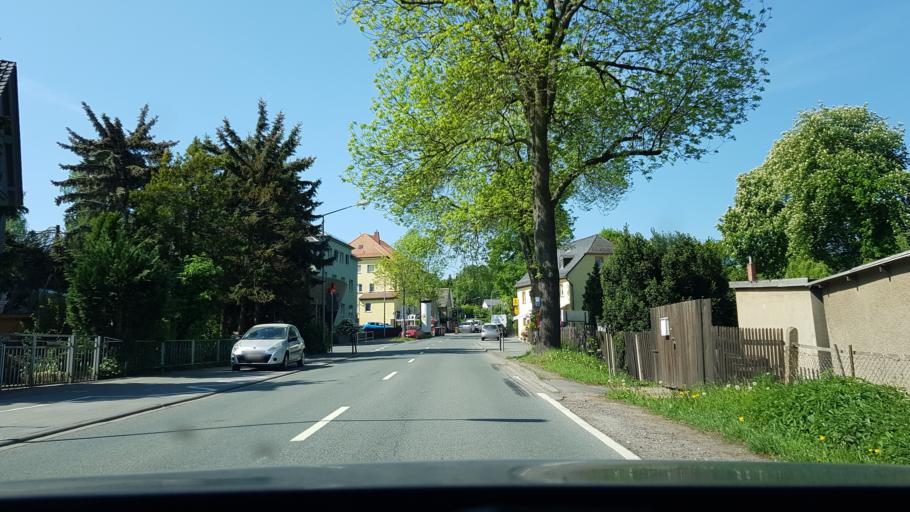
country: DE
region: Saxony
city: Wittgensdorf
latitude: 50.8580
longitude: 12.8873
